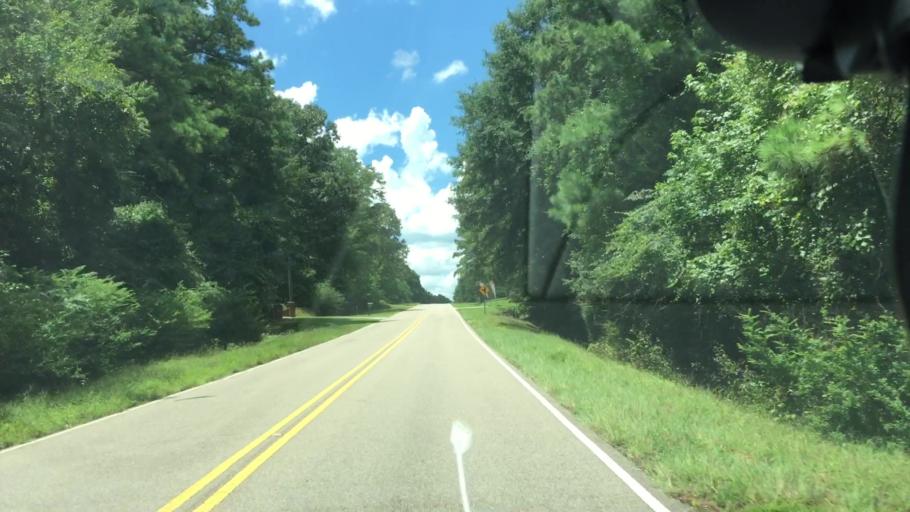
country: US
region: Alabama
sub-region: Coffee County
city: New Brockton
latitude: 31.4090
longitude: -85.8456
